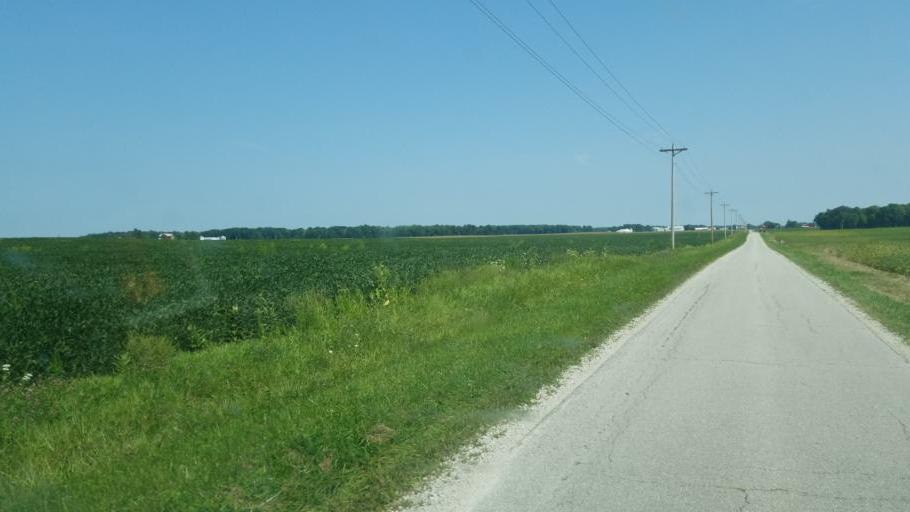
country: US
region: Ohio
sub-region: Crawford County
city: Bucyrus
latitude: 40.9358
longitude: -83.0254
